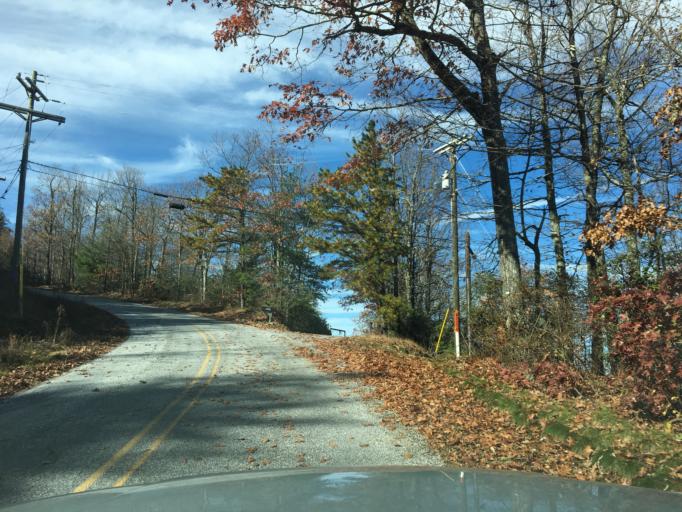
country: US
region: North Carolina
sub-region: Henderson County
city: Valley Hill
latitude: 35.2335
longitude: -82.5298
